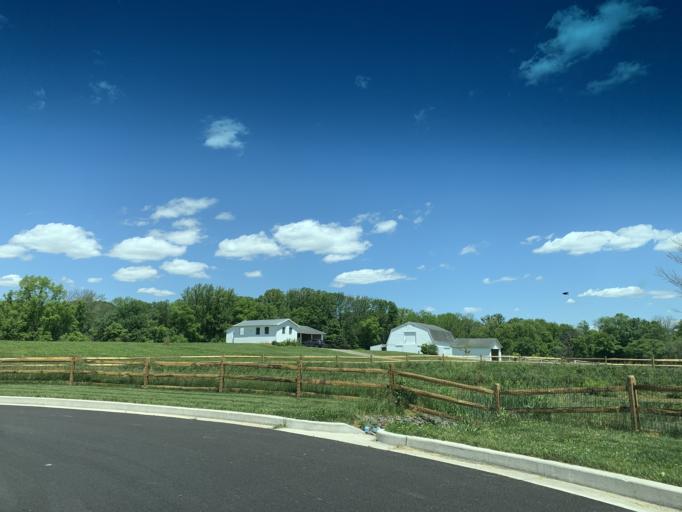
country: US
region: Maryland
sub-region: Cecil County
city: Rising Sun
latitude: 39.6909
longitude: -76.0124
